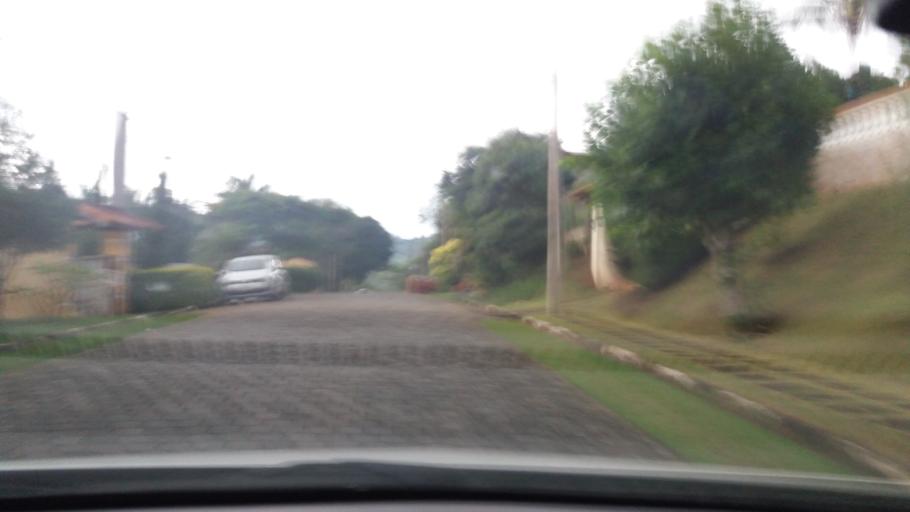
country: BR
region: Sao Paulo
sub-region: Bom Jesus Dos Perdoes
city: Bom Jesus dos Perdoes
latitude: -23.1660
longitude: -46.4573
